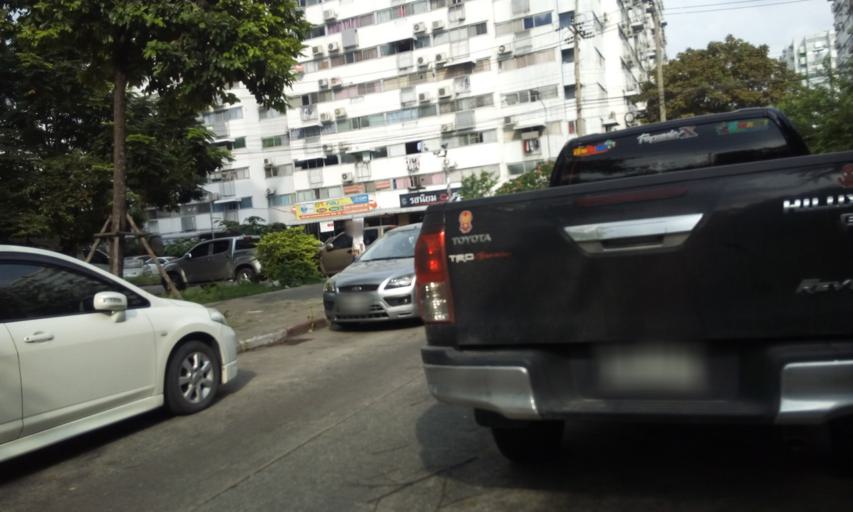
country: TH
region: Bangkok
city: Don Mueang
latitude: 13.9158
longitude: 100.5553
